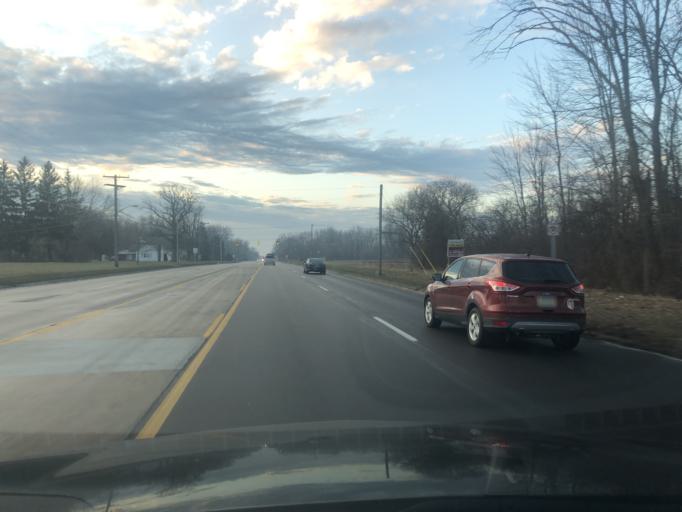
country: US
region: Michigan
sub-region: Wayne County
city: Wayne
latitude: 42.2616
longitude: -83.3480
